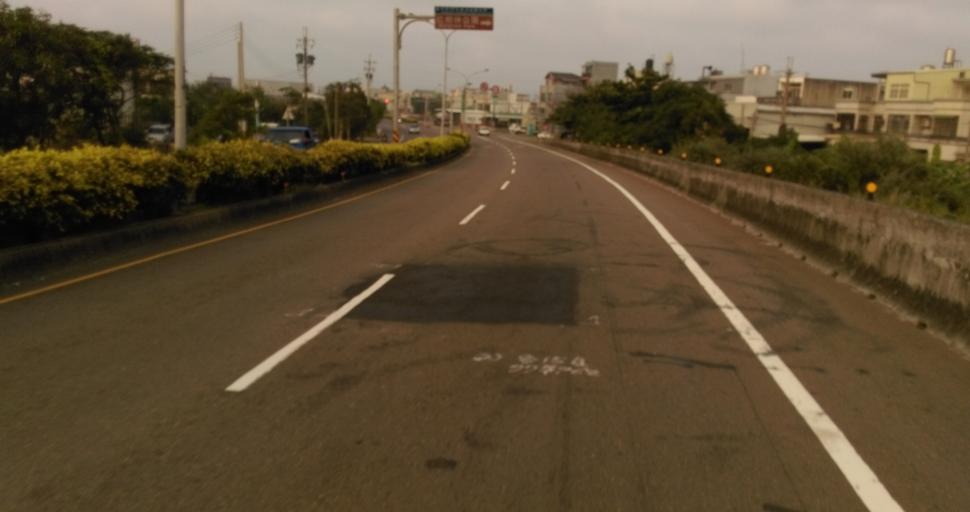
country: TW
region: Taiwan
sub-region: Hsinchu
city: Hsinchu
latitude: 24.8113
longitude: 120.9212
